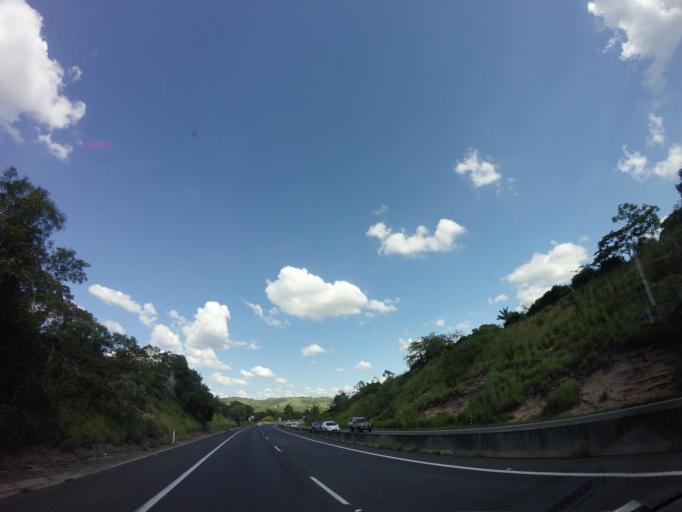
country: AU
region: Queensland
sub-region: Ipswich
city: Thagoona
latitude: -27.5515
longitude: 152.5349
